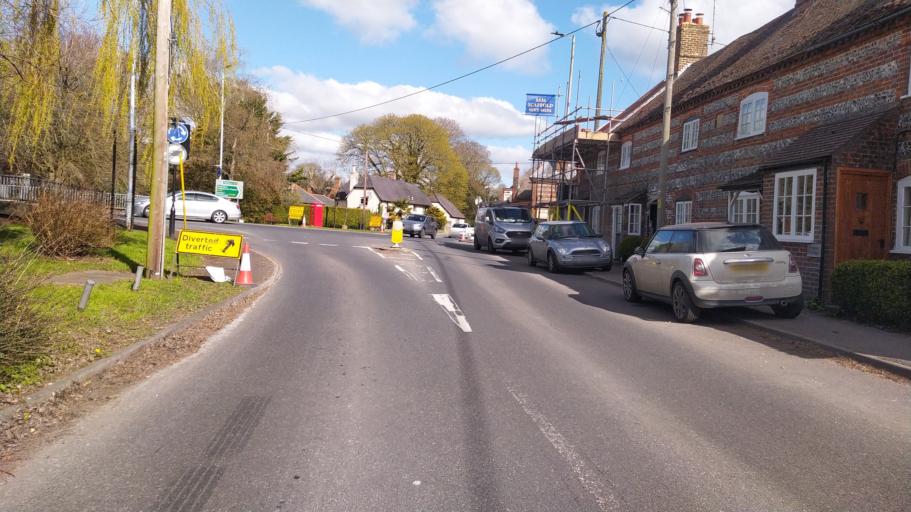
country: GB
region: England
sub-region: Wiltshire
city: Collingbourne Kingston
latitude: 51.2820
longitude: -1.6514
